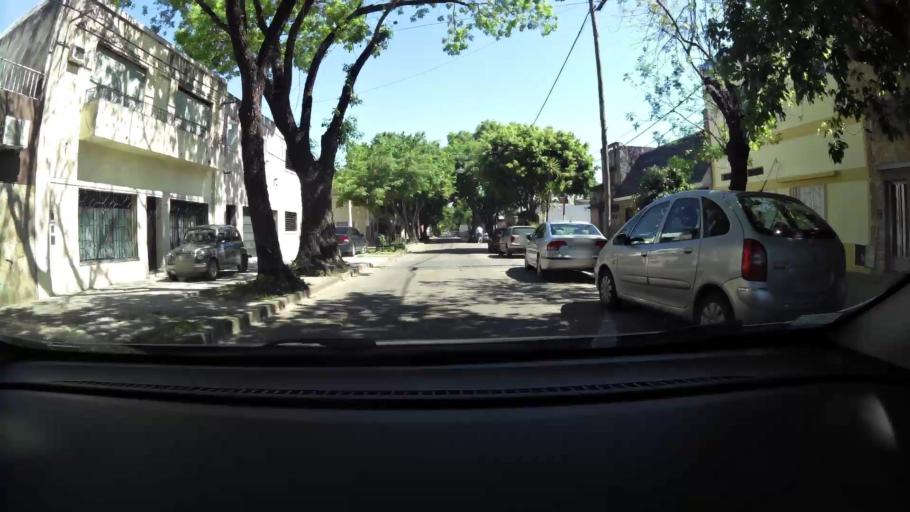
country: AR
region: Santa Fe
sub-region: Departamento de Rosario
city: Rosario
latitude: -32.9400
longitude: -60.6822
